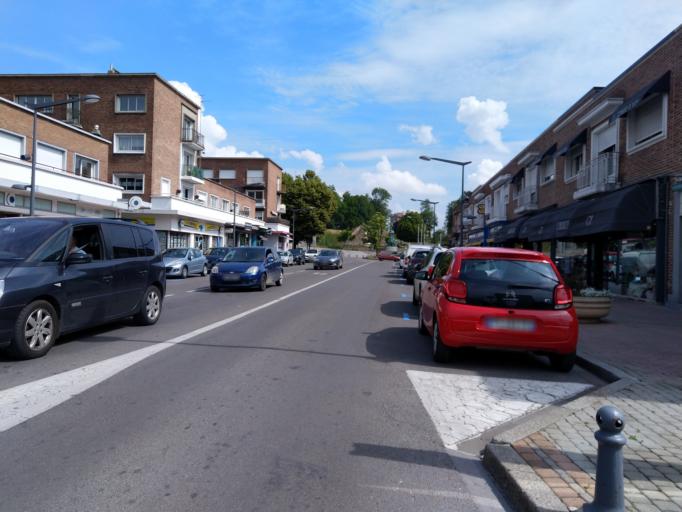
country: FR
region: Nord-Pas-de-Calais
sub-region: Departement du Nord
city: Maubeuge
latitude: 50.2788
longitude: 3.9740
